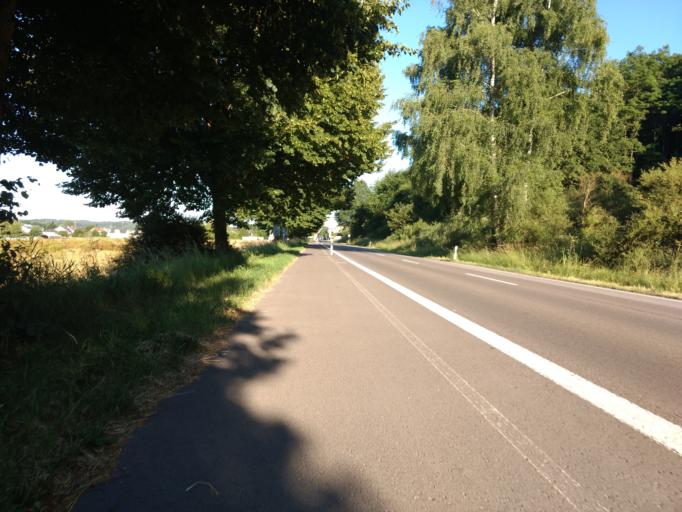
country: DE
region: Saarland
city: Rehlingen-Siersburg
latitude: 49.3839
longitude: 6.6691
